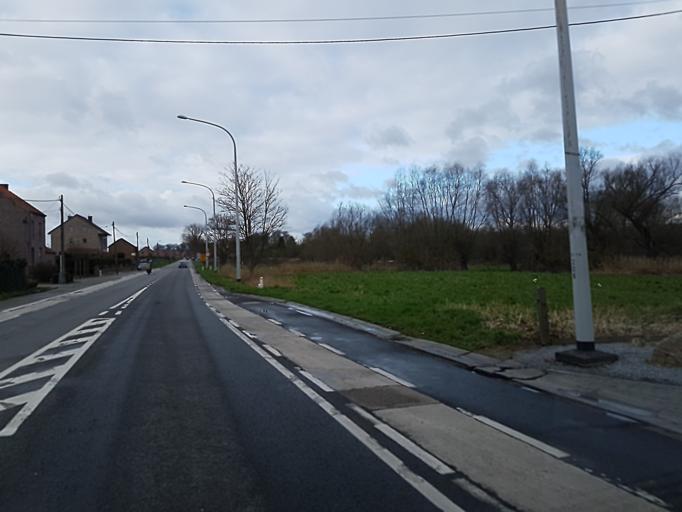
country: BE
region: Flanders
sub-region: Provincie Vlaams-Brabant
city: Hoegaarden
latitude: 50.7681
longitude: 4.9075
